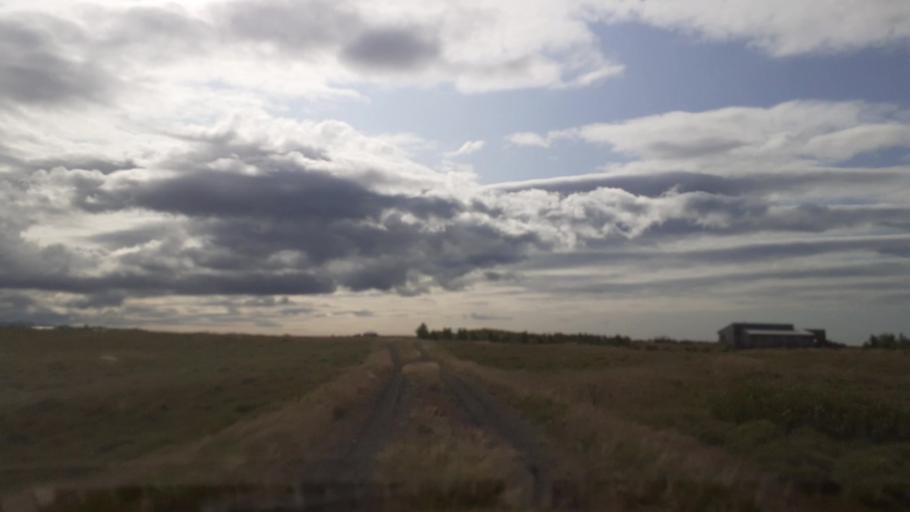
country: IS
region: South
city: Vestmannaeyjar
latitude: 63.7749
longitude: -20.3001
